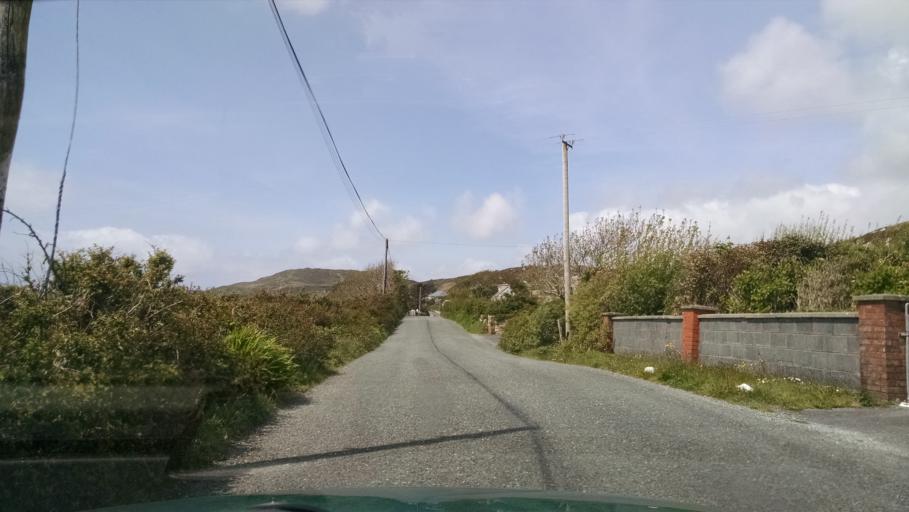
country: IE
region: Connaught
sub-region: County Galway
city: Clifden
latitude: 53.4900
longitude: -10.0438
